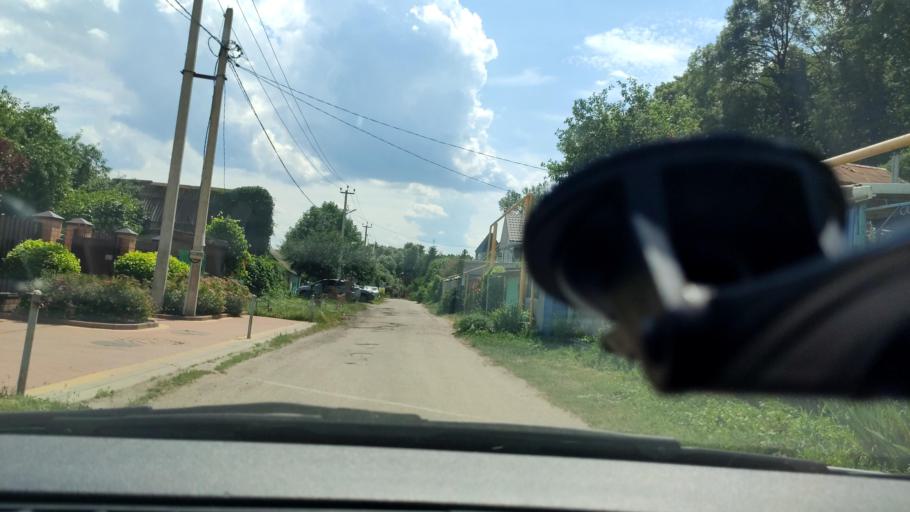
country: RU
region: Voronezj
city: Ramon'
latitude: 51.8927
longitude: 39.3429
